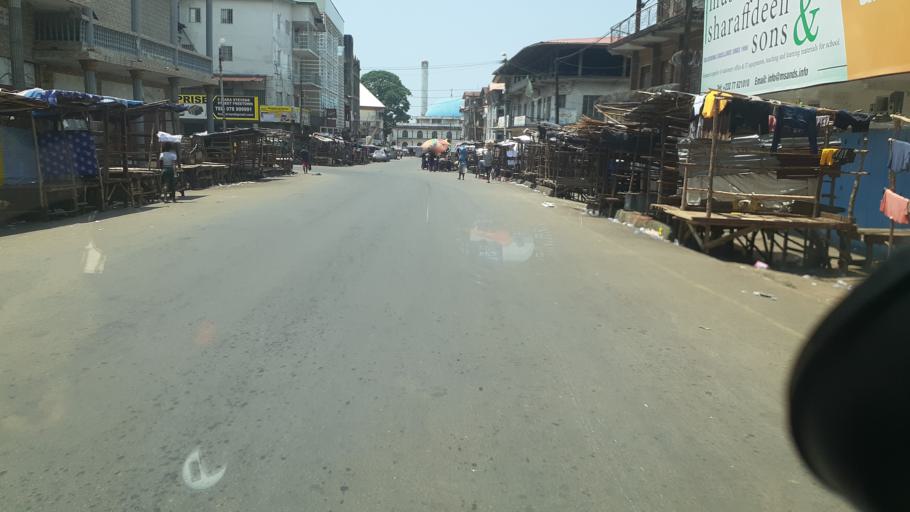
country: SL
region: Western Area
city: Freetown
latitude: 8.4898
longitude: -13.2313
